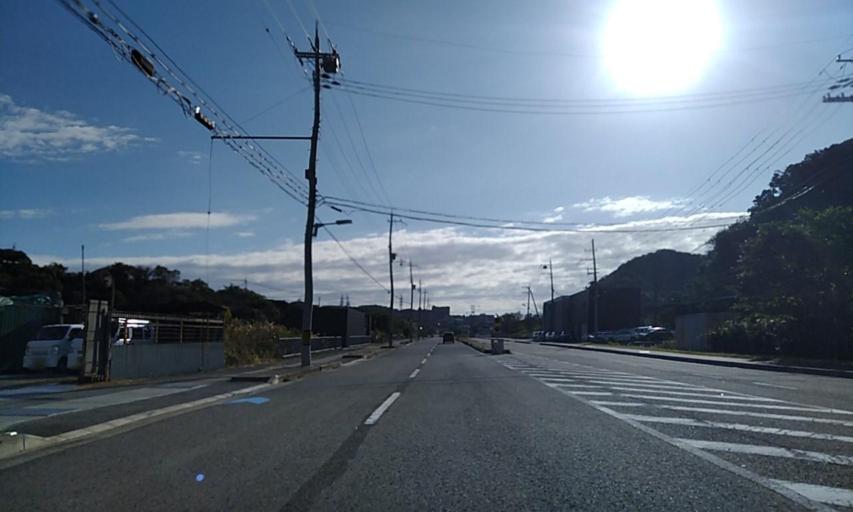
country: JP
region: Wakayama
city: Minato
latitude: 34.2697
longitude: 135.0865
